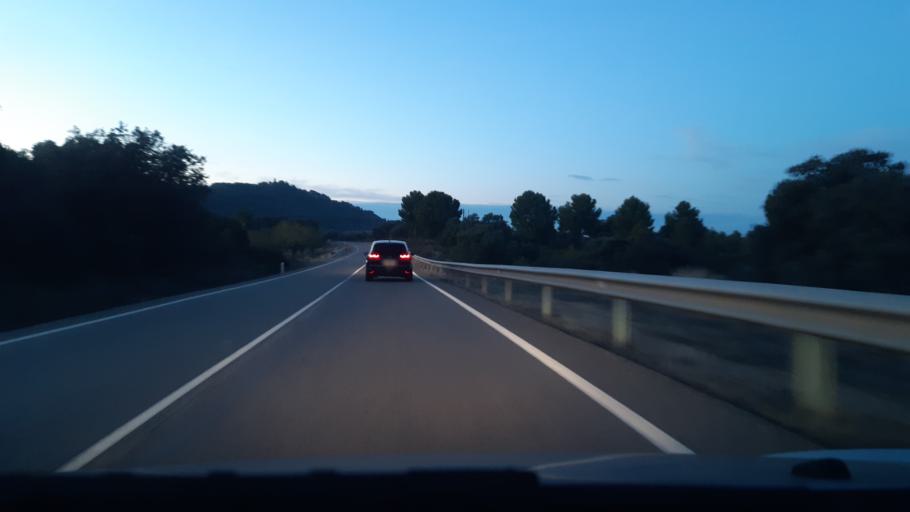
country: ES
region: Aragon
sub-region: Provincia de Teruel
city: Calaceite
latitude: 40.9993
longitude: 0.1954
